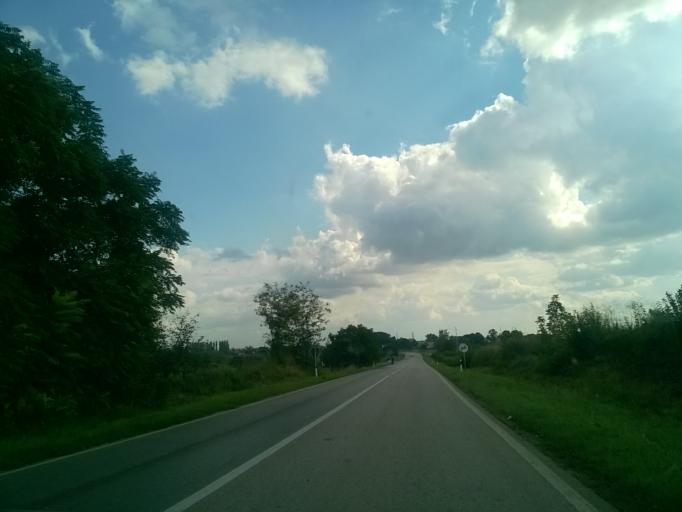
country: RS
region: Autonomna Pokrajina Vojvodina
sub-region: Juznobanatski Okrug
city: Vrsac
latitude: 45.1311
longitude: 21.2715
